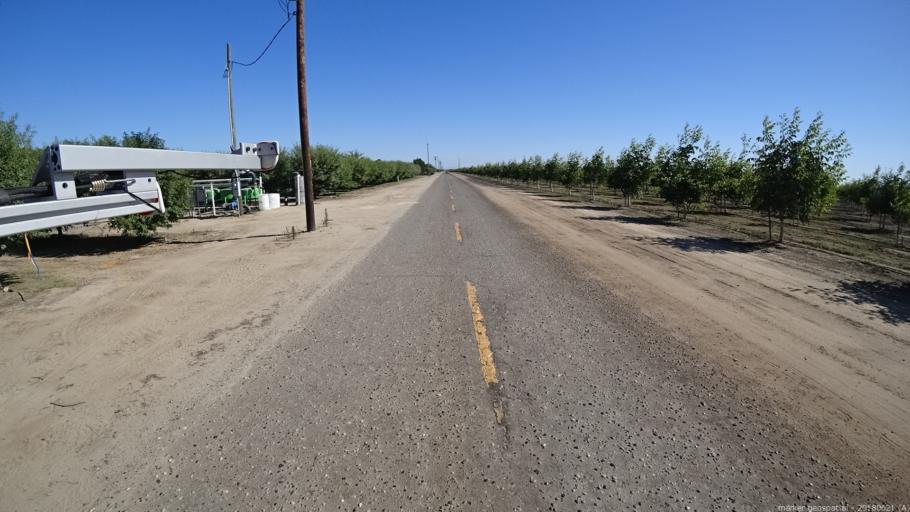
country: US
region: California
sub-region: Fresno County
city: Biola
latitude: 36.8468
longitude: -120.0464
